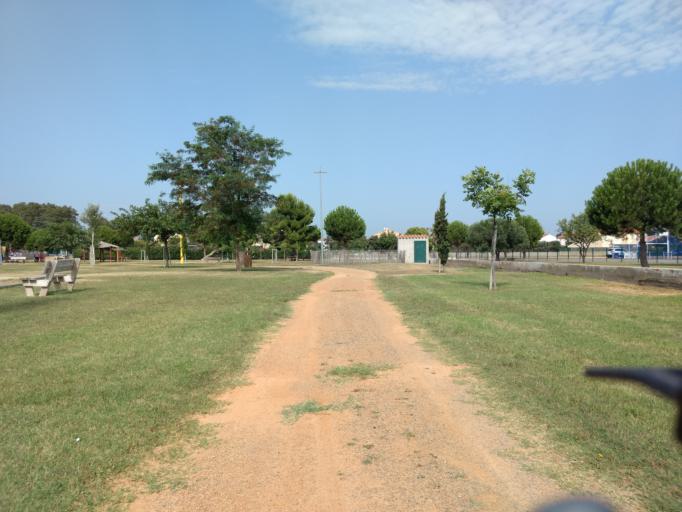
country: FR
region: Languedoc-Roussillon
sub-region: Departement des Pyrenees-Orientales
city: Saint-Laurent-de-la-Salanque
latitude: 42.7663
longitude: 2.9907
